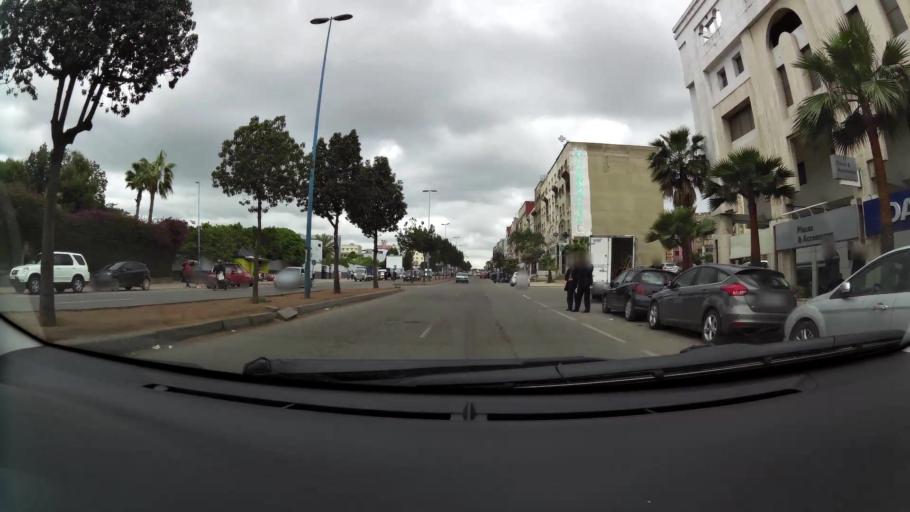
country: MA
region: Grand Casablanca
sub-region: Casablanca
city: Casablanca
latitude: 33.5639
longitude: -7.5546
